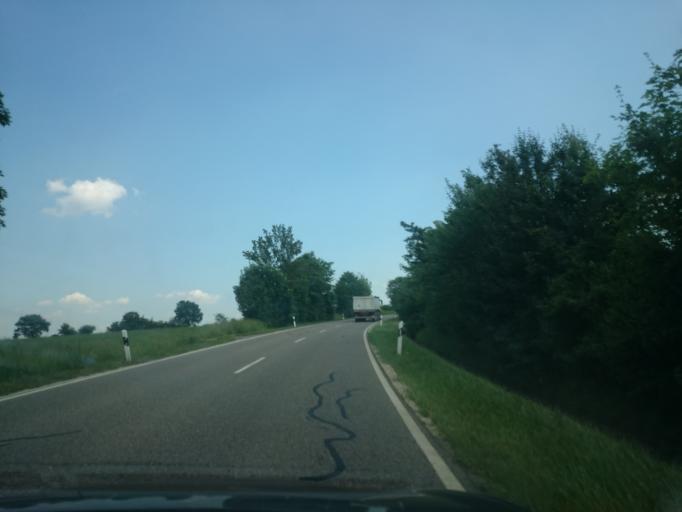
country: DE
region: Bavaria
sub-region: Regierungsbezirk Mittelfranken
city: Hilpoltstein
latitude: 49.1864
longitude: 11.2037
